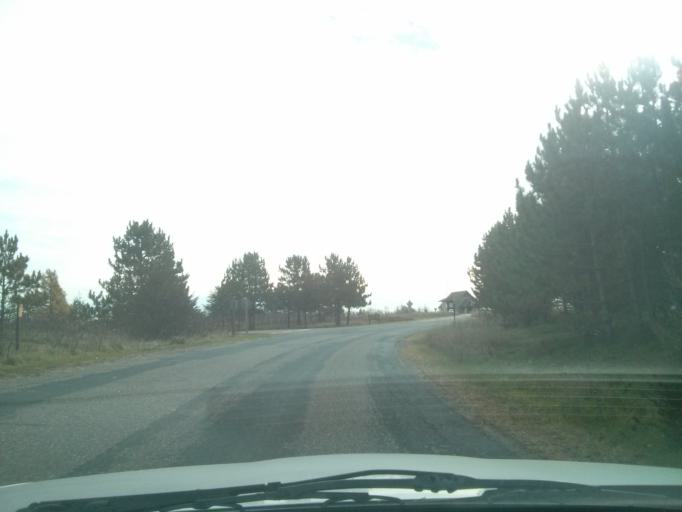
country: US
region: Wisconsin
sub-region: Saint Croix County
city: North Hudson
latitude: 45.0137
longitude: -92.6809
